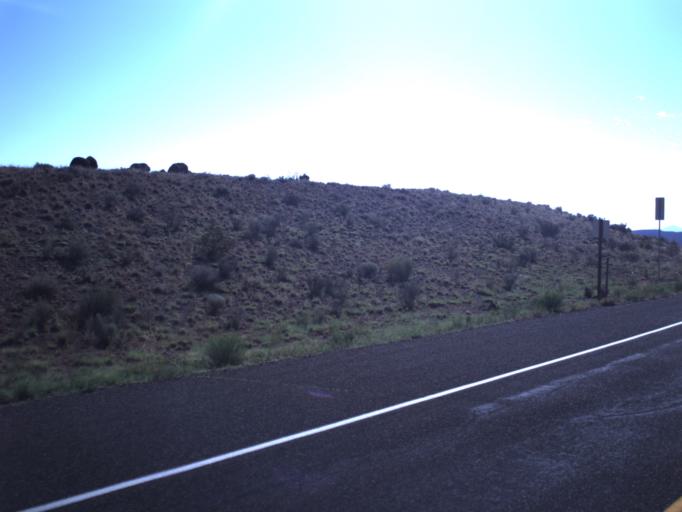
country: US
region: Utah
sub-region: Wayne County
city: Loa
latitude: 38.2977
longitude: -111.3991
